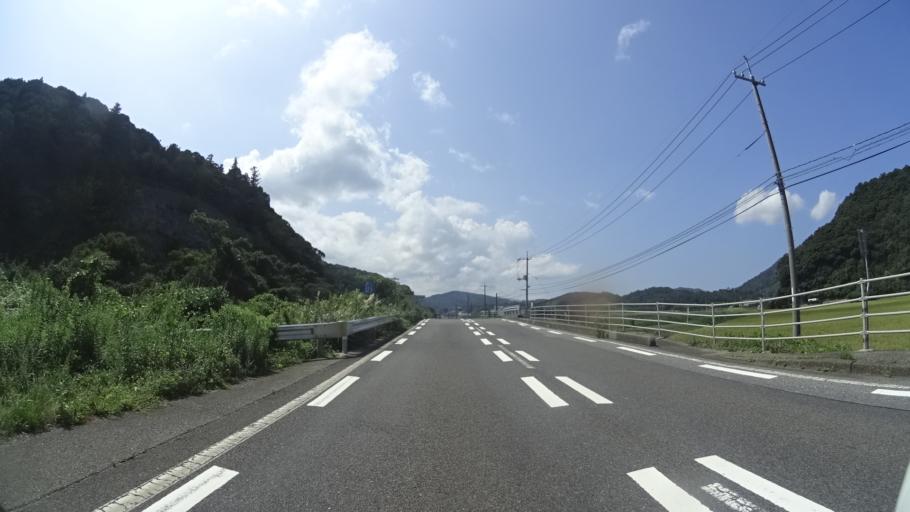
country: JP
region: Shimane
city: Masuda
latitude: 34.6528
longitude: 131.6689
